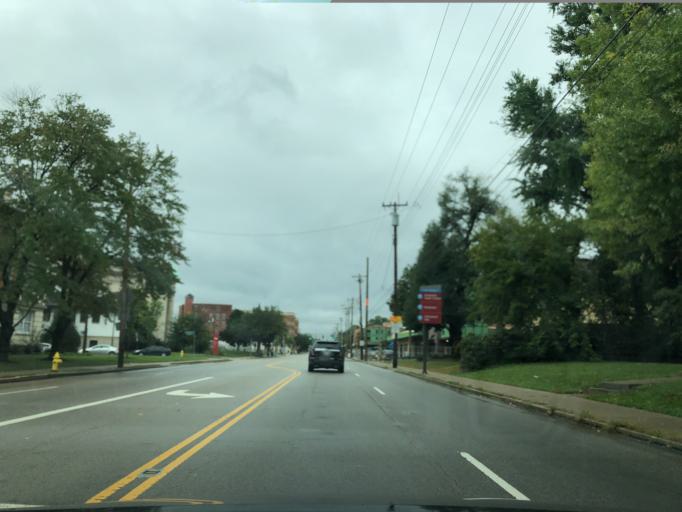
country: US
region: Ohio
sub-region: Hamilton County
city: Saint Bernard
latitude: 39.1478
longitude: -84.4890
